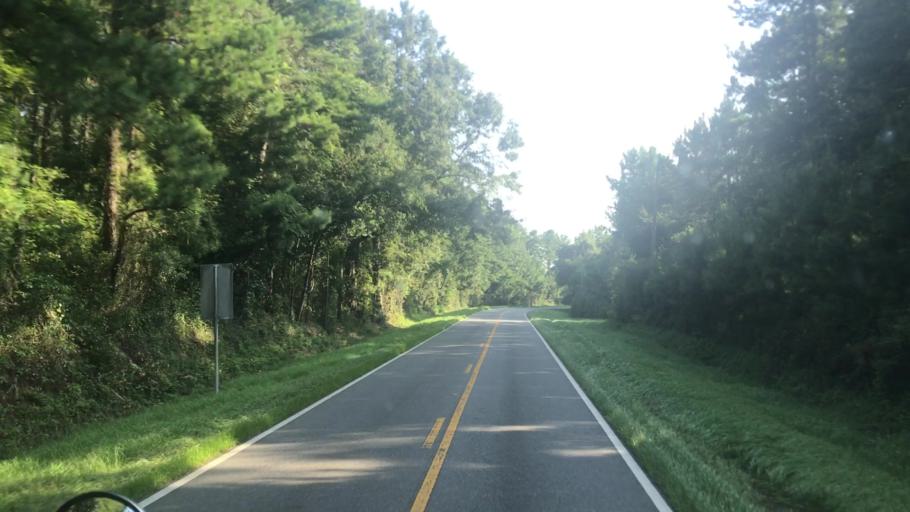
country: US
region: Florida
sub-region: Gadsden County
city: Quincy
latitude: 30.6944
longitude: -84.5379
